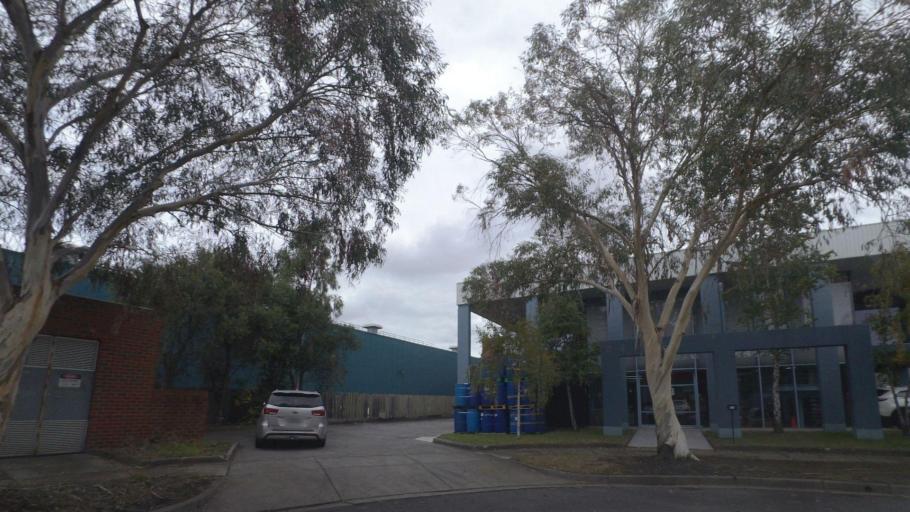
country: AU
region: Victoria
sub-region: Whitehorse
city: Nunawading
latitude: -37.8191
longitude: 145.1662
